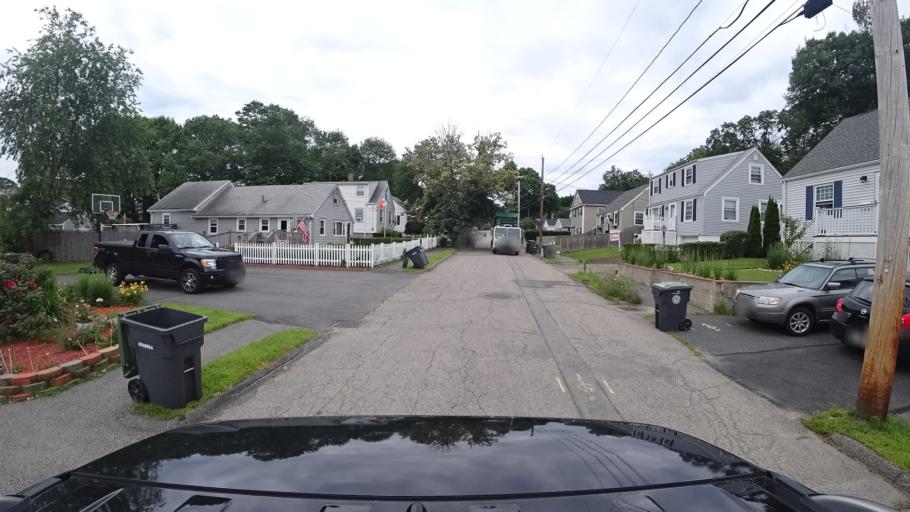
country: US
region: Massachusetts
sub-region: Norfolk County
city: Dedham
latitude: 42.2350
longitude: -71.1466
